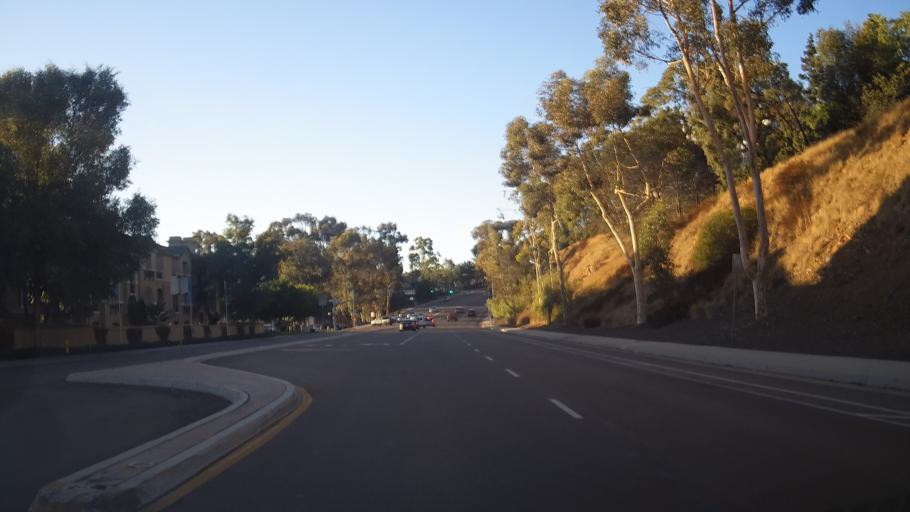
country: US
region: California
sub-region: San Diego County
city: Poway
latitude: 32.9155
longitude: -117.1106
